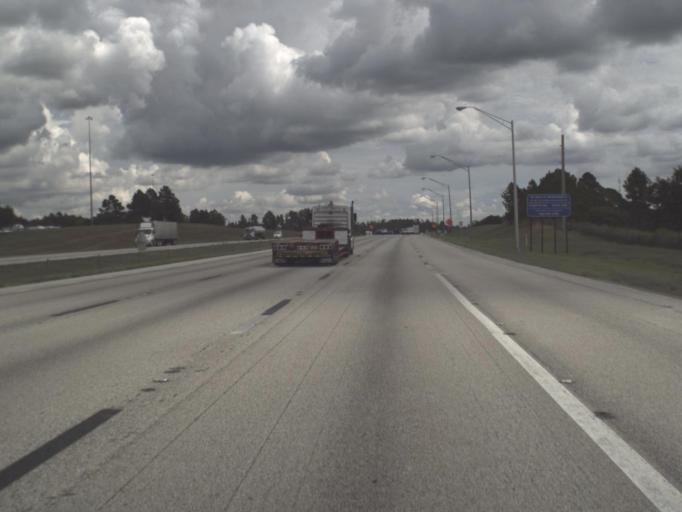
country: US
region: Florida
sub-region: Polk County
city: Polk City
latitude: 28.1709
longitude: -81.7685
